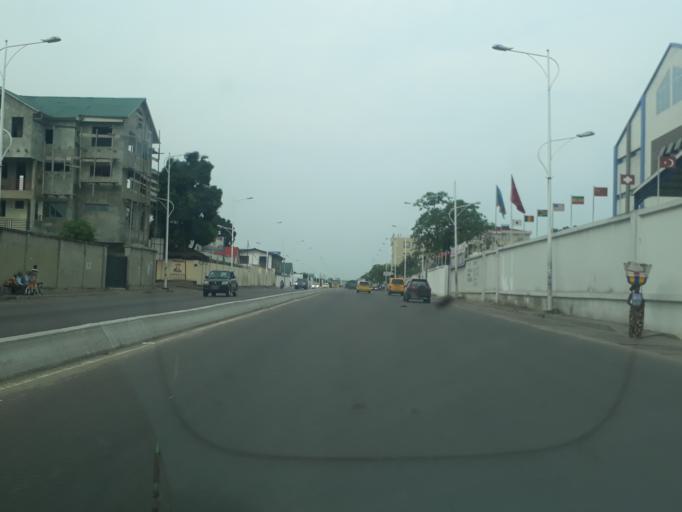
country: CD
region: Kinshasa
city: Kinshasa
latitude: -4.3327
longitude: 15.2624
